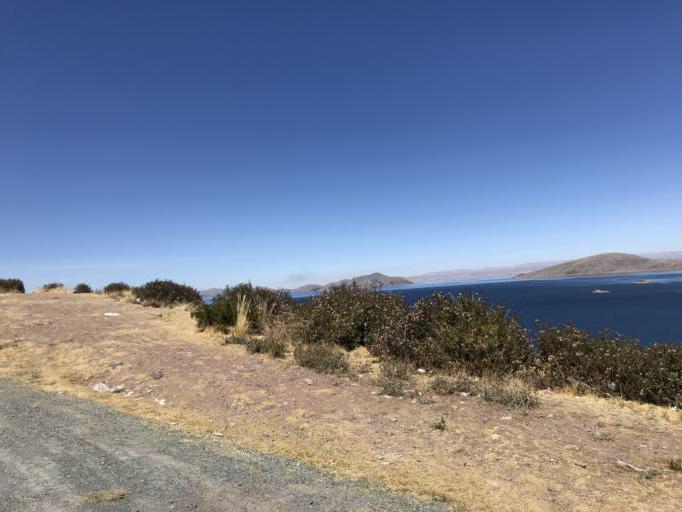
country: BO
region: La Paz
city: San Pablo
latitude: -16.2188
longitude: -68.8330
